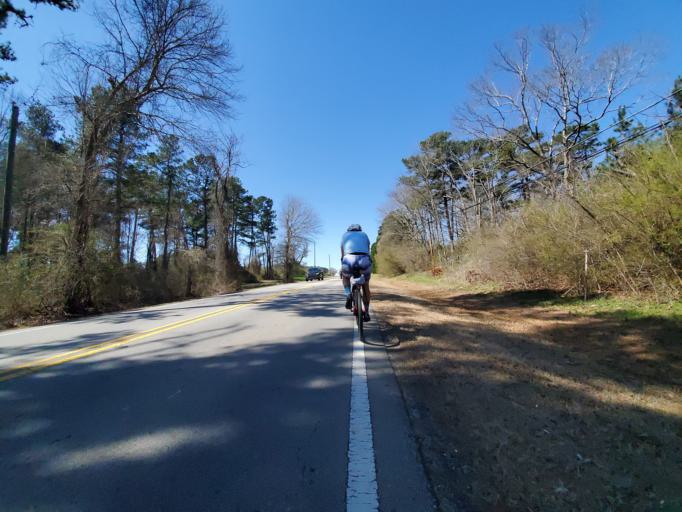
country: US
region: Georgia
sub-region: Barrow County
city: Russell
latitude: 33.9982
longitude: -83.6942
